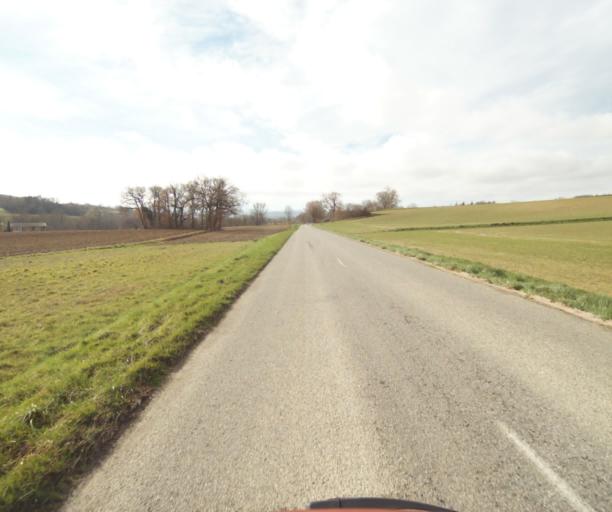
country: FR
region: Midi-Pyrenees
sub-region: Departement de l'Ariege
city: Pamiers
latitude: 43.1353
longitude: 1.5592
